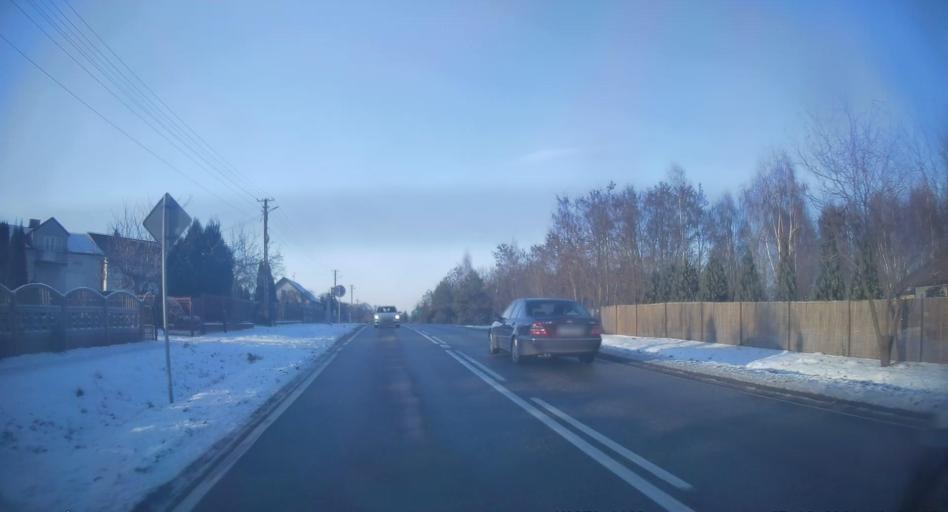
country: PL
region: Lodz Voivodeship
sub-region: Powiat opoczynski
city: Zarnow
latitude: 51.2518
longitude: 20.1704
